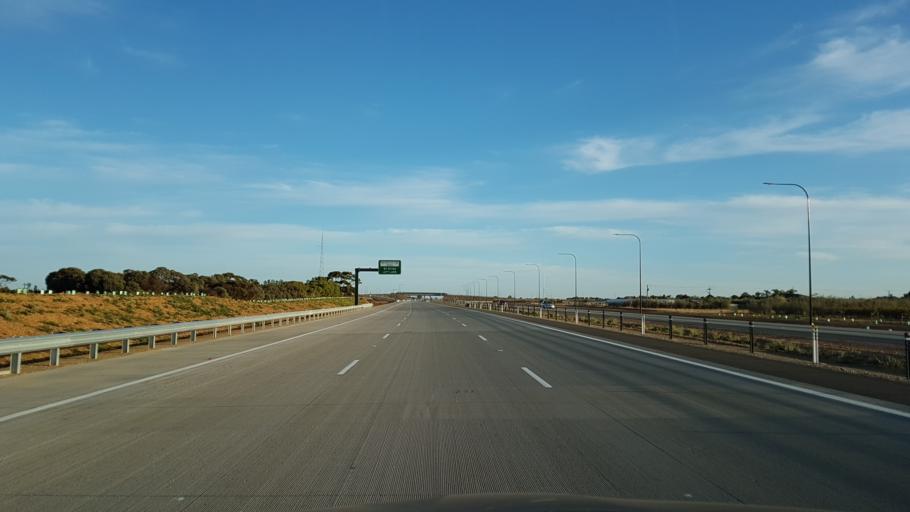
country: AU
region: South Australia
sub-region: Salisbury
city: Salisbury
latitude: -34.7418
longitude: 138.5796
